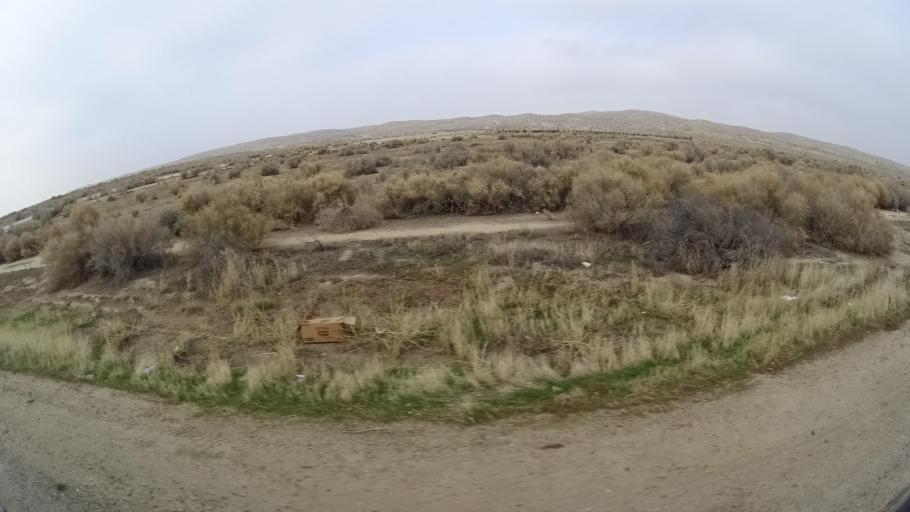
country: US
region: California
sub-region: Kern County
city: South Taft
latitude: 35.1301
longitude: -119.3874
